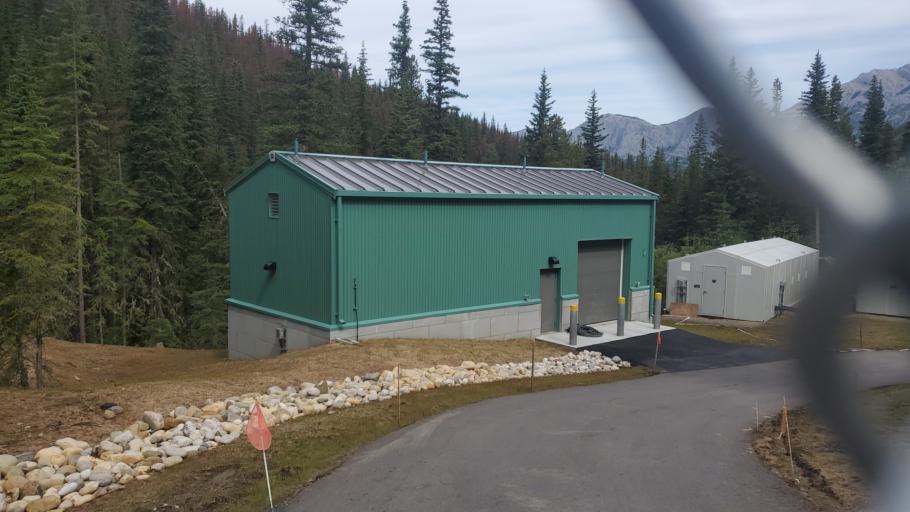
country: CA
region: Alberta
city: Hinton
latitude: 53.1290
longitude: -117.7735
